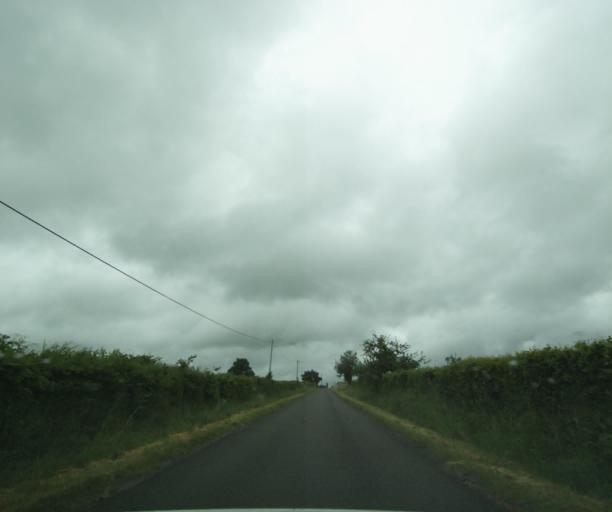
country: FR
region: Bourgogne
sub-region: Departement de Saone-et-Loire
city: Charolles
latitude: 46.4577
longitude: 4.4330
